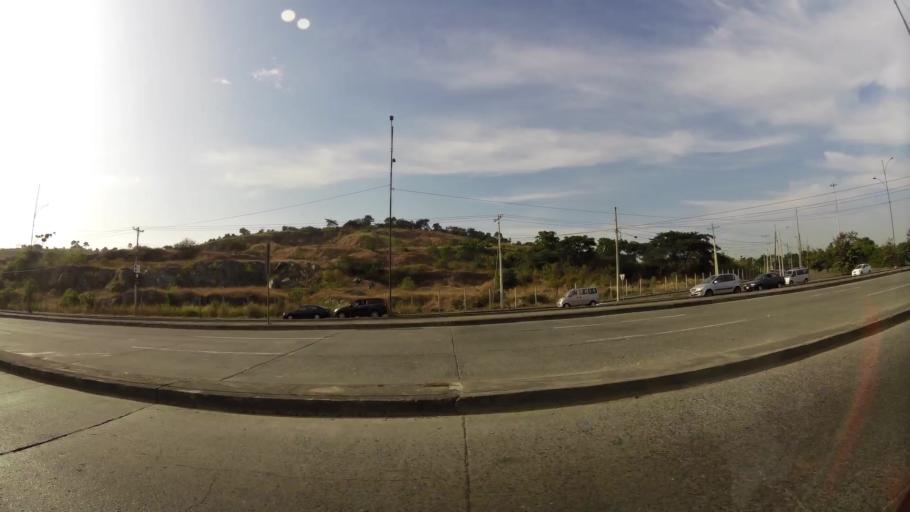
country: EC
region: Guayas
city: Eloy Alfaro
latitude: -2.0721
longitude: -79.9172
